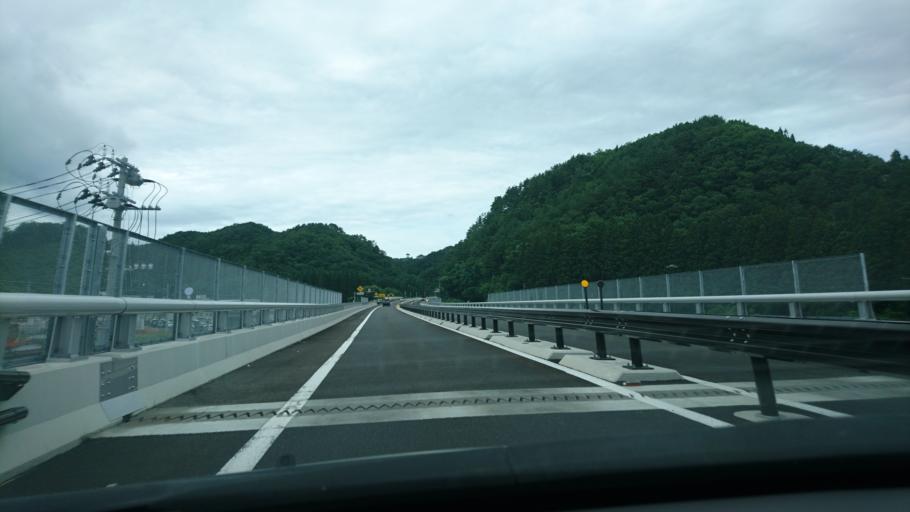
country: JP
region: Iwate
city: Miyako
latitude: 39.8415
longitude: 141.9557
